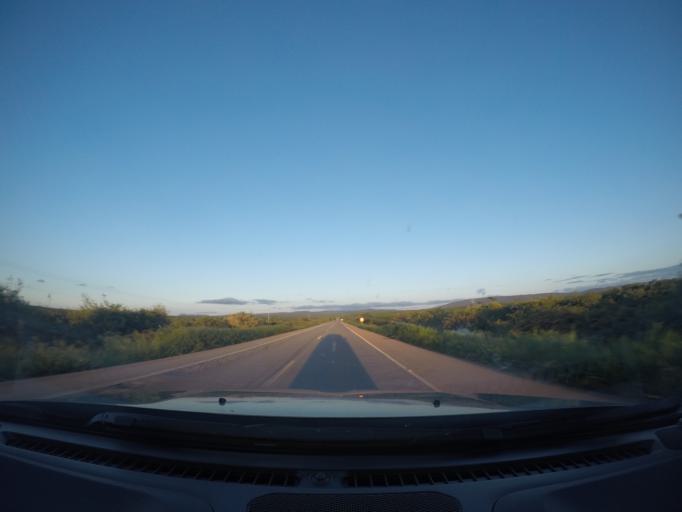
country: BR
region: Bahia
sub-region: Seabra
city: Seabra
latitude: -12.3994
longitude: -41.9412
